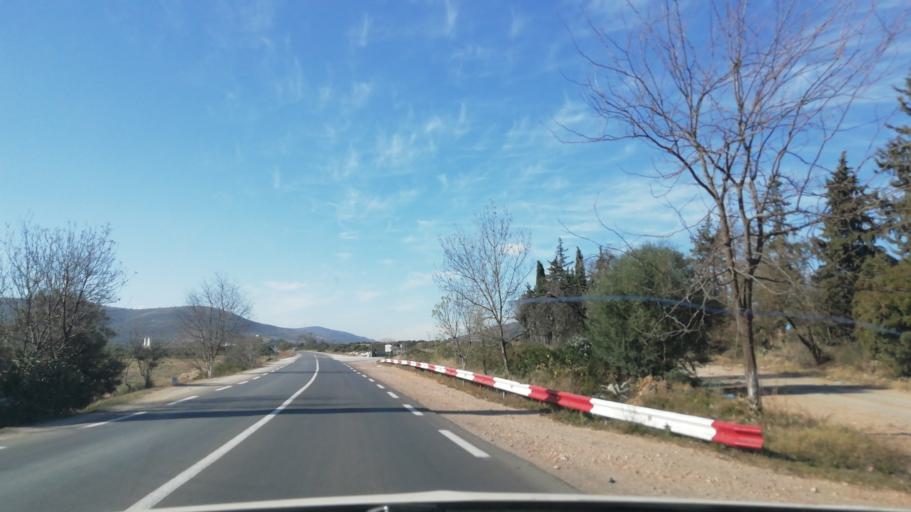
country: DZ
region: Tlemcen
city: Ouled Mimoun
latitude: 34.8688
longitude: -1.1572
